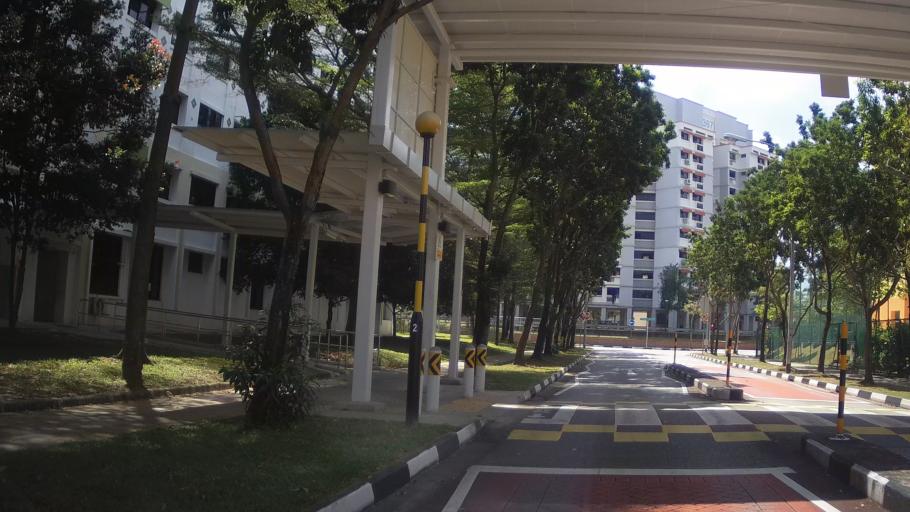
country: MY
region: Johor
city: Johor Bahru
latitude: 1.3385
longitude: 103.7179
